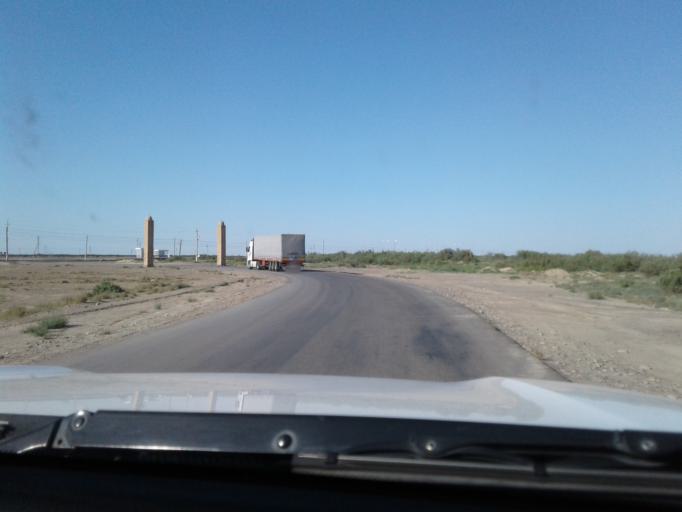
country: IR
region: Razavi Khorasan
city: Kalat-e Naderi
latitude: 37.2013
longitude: 60.0419
